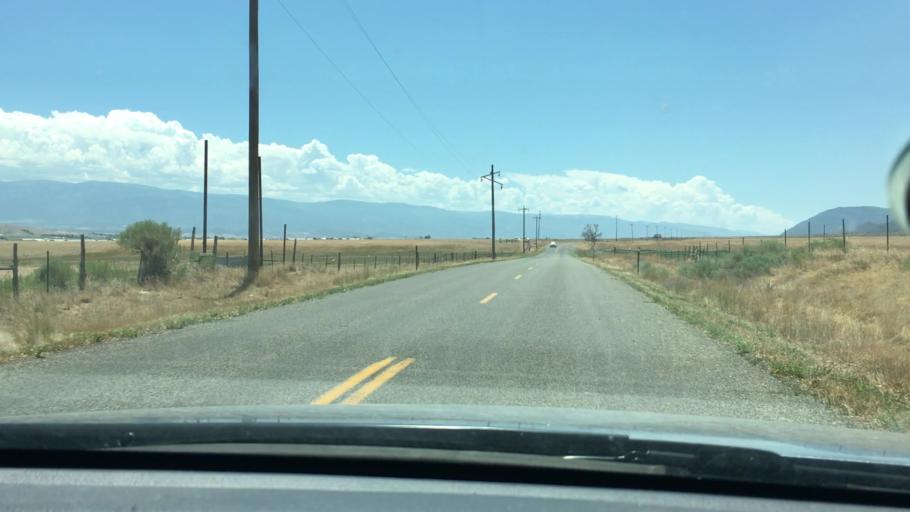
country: US
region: Utah
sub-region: Sanpete County
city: Fountain Green
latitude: 39.5854
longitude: -111.6413
